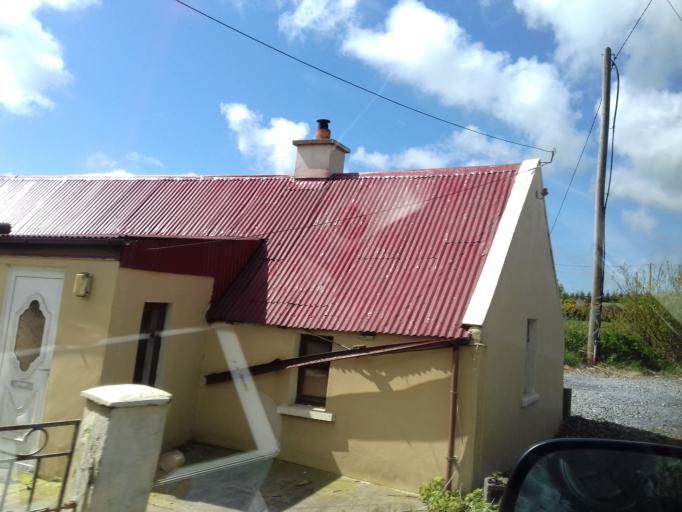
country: IE
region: Leinster
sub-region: Loch Garman
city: Loch Garman
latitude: 52.2836
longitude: -6.6476
